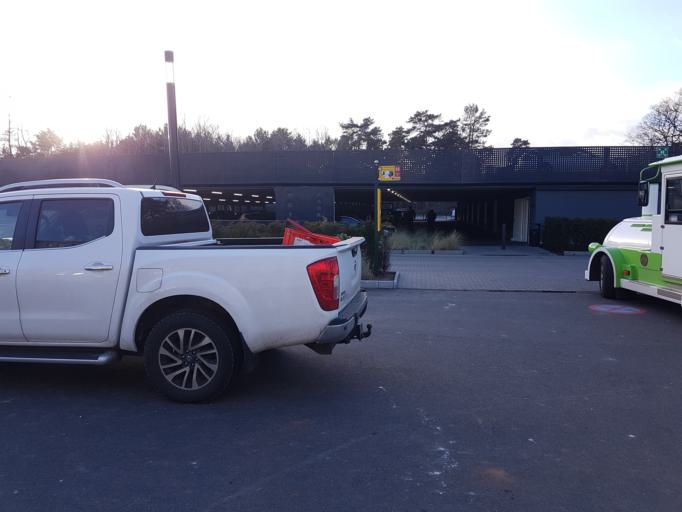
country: DE
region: Mecklenburg-Vorpommern
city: Ostseebad Binz
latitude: 54.4310
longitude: 13.5803
